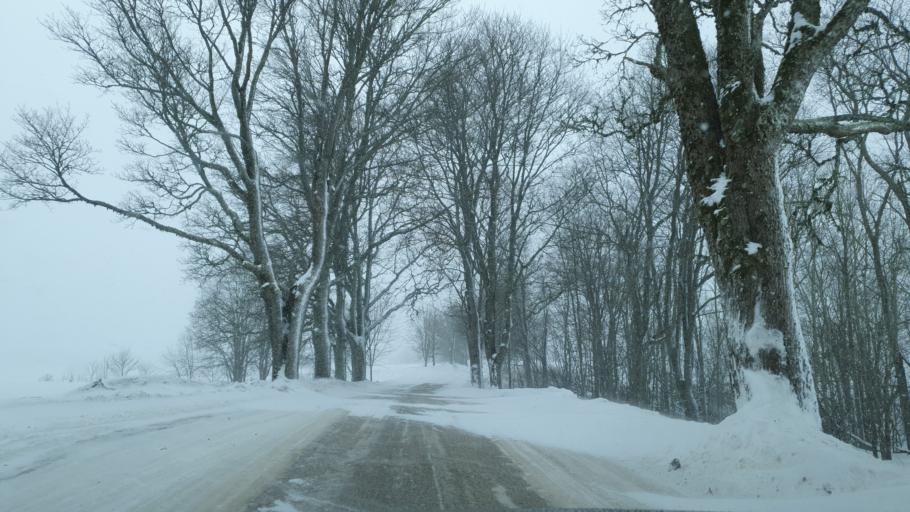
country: EE
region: Jogevamaa
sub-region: Jogeva linn
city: Jogeva
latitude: 58.7441
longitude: 26.5245
